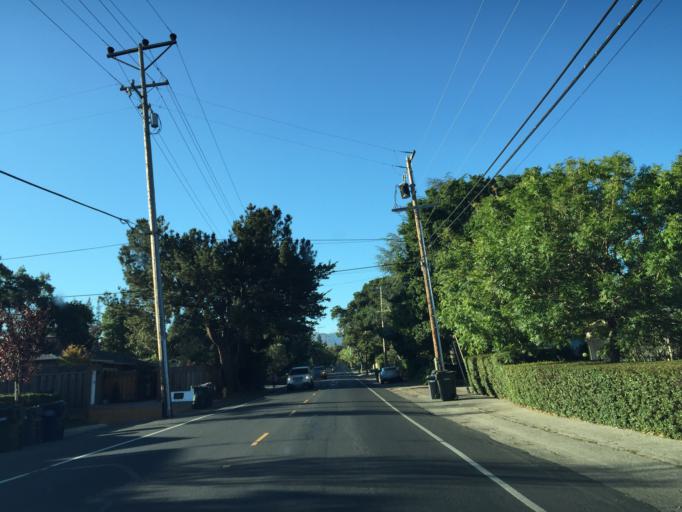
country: US
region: California
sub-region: Santa Clara County
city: Los Altos
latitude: 37.3870
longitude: -122.1208
